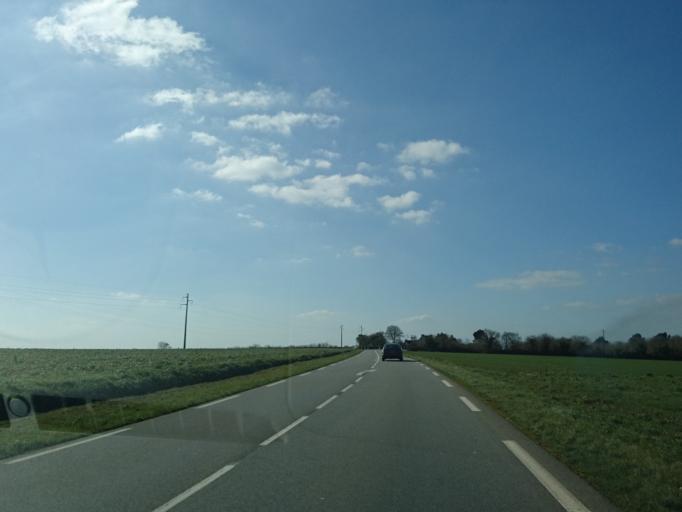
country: FR
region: Brittany
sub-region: Departement du Finistere
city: Telgruc-sur-Mer
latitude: 48.2620
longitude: -4.3128
